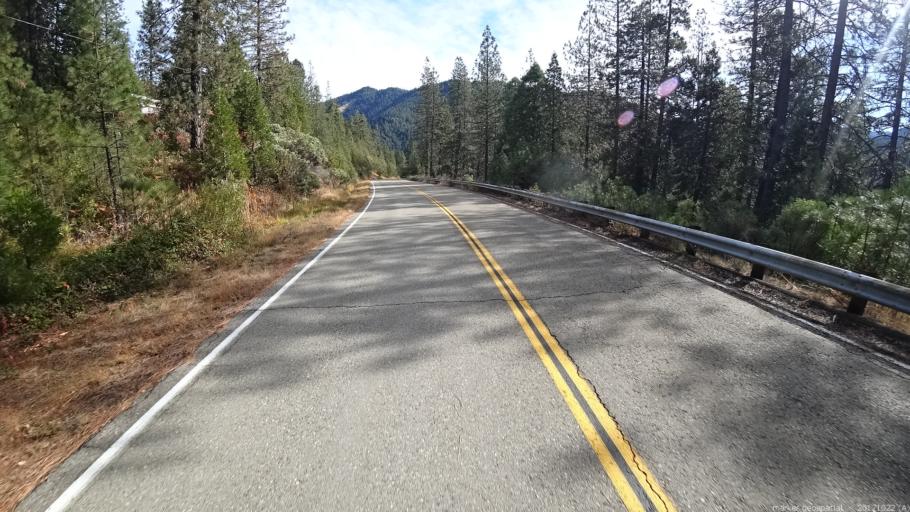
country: US
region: California
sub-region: Siskiyou County
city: Dunsmuir
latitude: 41.0646
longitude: -122.3693
